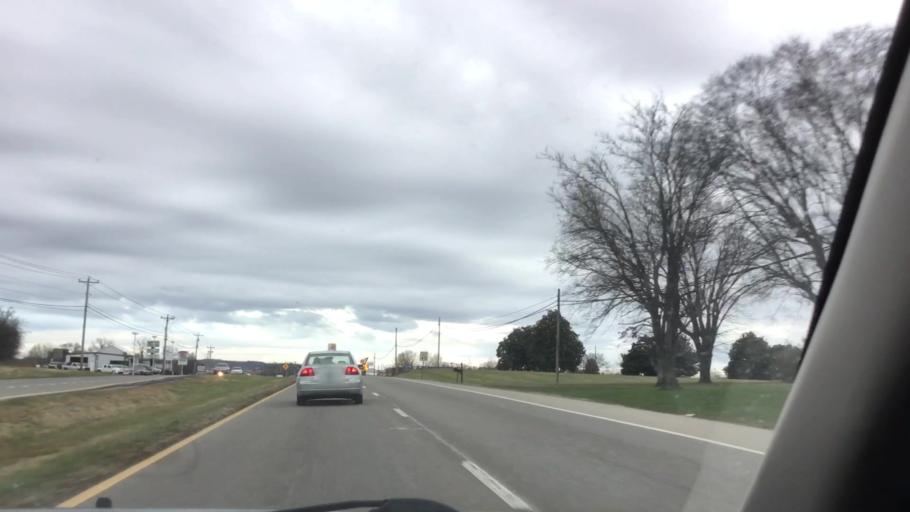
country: US
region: Tennessee
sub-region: Maury County
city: Spring Hill
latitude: 35.7064
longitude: -86.9764
